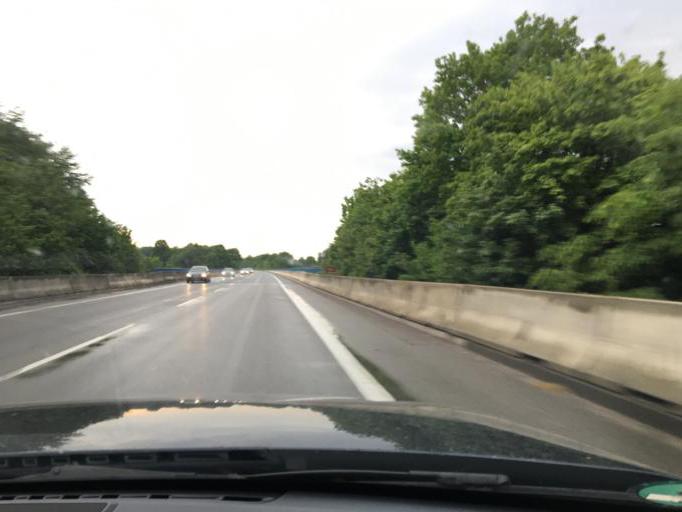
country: DE
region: North Rhine-Westphalia
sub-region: Regierungsbezirk Munster
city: Greven
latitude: 52.1192
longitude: 7.5984
